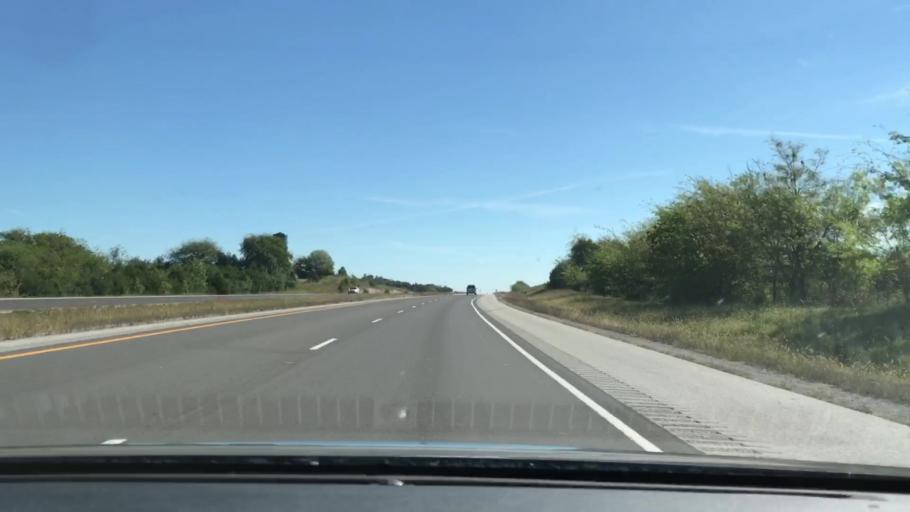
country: US
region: Kentucky
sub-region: Logan County
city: Russellville
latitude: 36.8368
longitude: -86.9552
